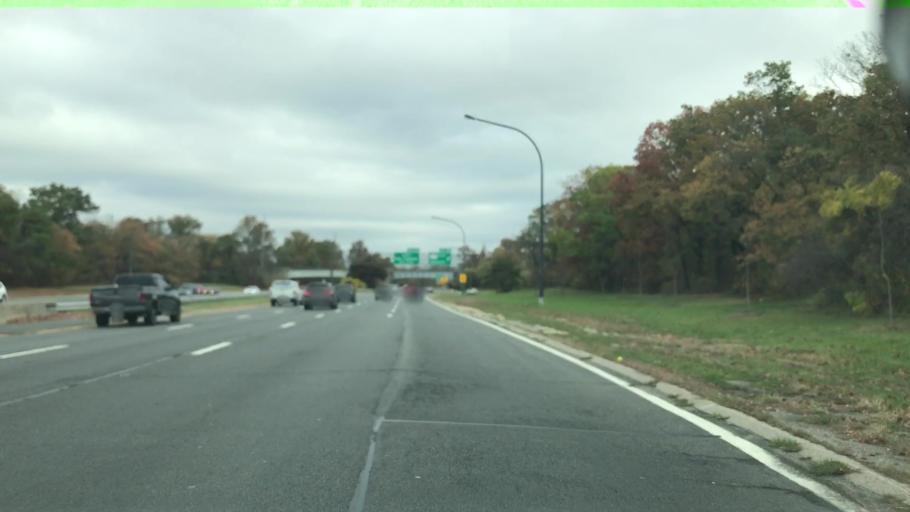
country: US
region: New York
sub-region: Suffolk County
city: East Farmingdale
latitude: 40.7153
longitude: -73.4096
